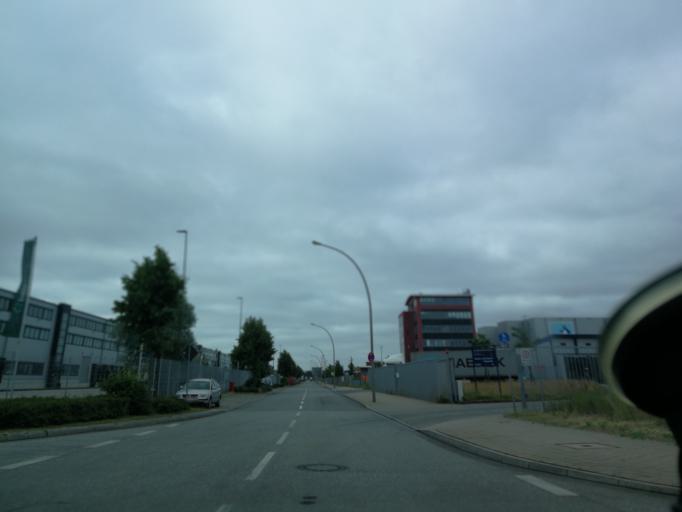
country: DE
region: Hamburg
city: Altona
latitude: 53.5084
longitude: 9.9215
